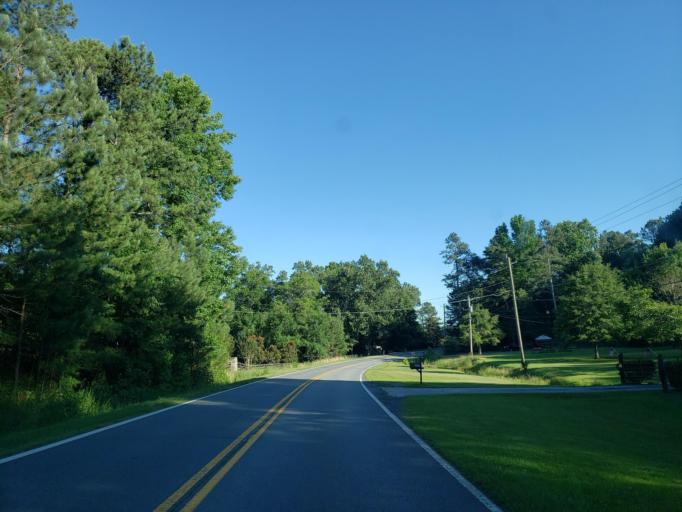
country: US
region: Georgia
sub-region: Floyd County
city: Shannon
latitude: 34.3731
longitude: -85.1318
